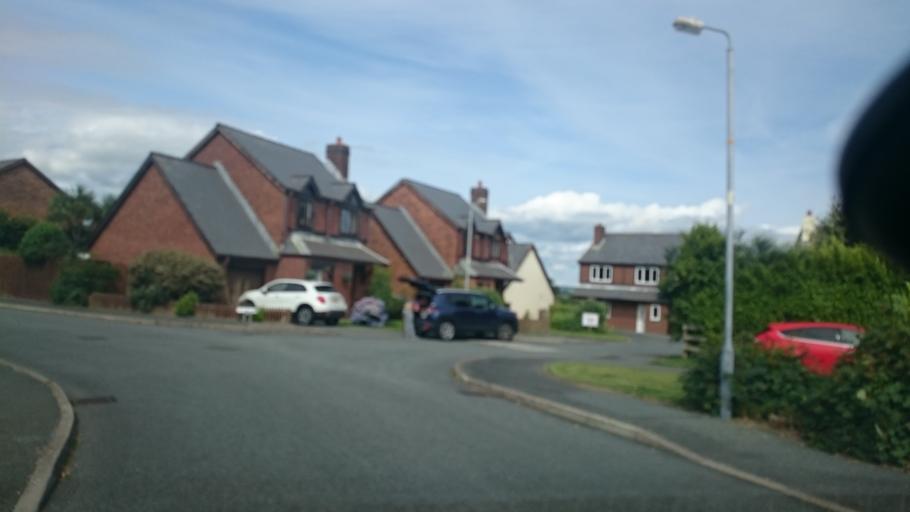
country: GB
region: Wales
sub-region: Pembrokeshire
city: Haverfordwest
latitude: 51.7861
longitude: -4.9702
